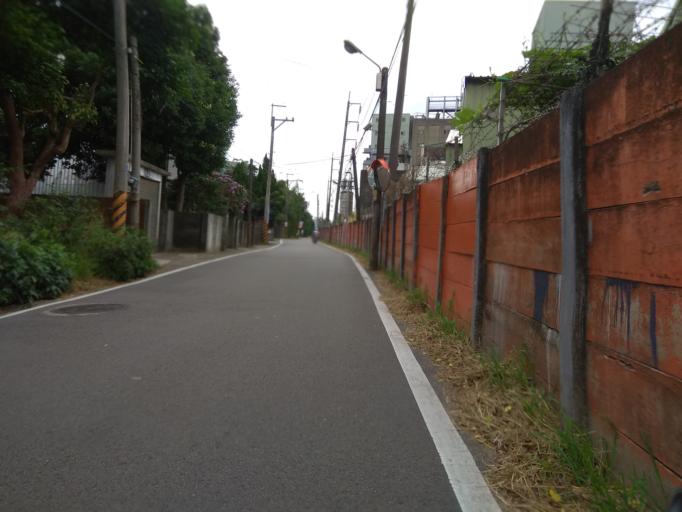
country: TW
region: Taiwan
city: Daxi
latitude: 24.9368
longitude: 121.2051
